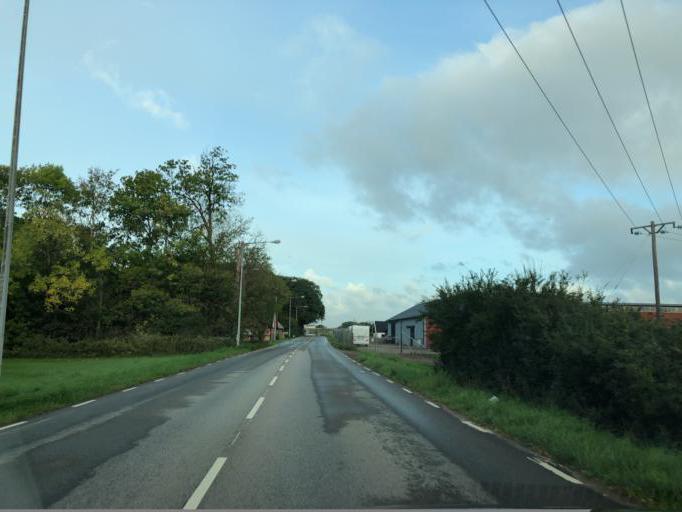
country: SE
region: Skane
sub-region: Landskrona
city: Asmundtorp
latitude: 55.8622
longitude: 12.8928
